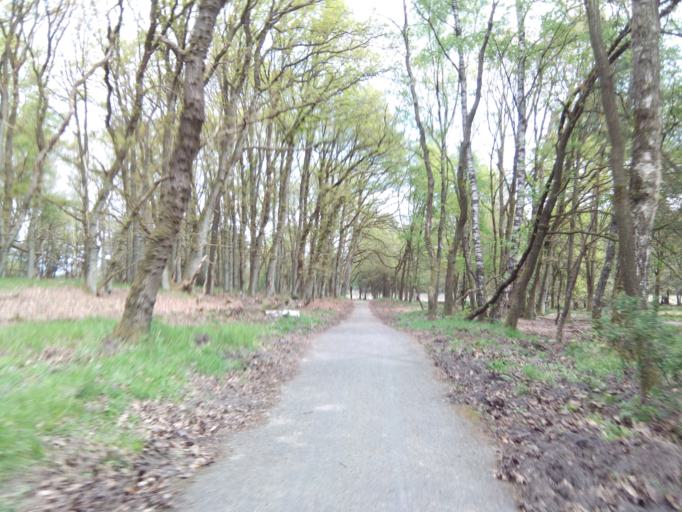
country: NL
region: Gelderland
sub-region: Gemeente Ede
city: Otterlo
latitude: 52.0637
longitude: 5.7614
